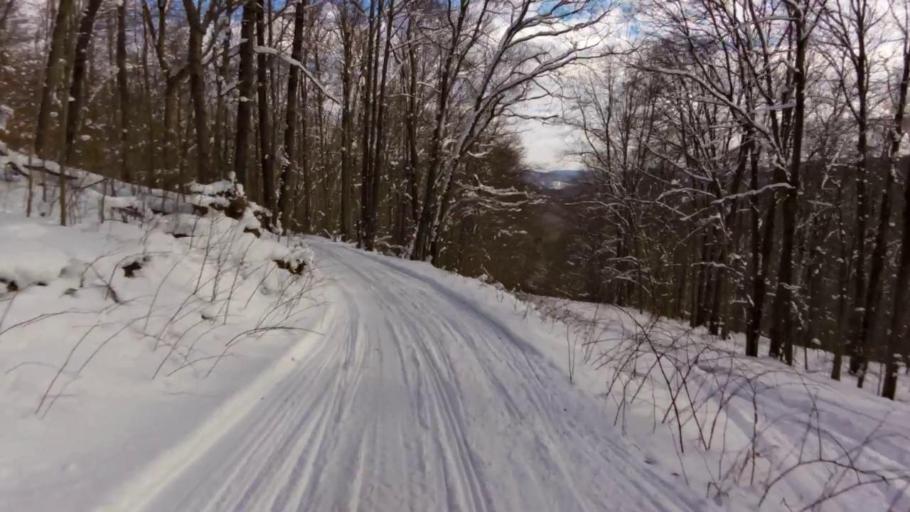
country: US
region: New York
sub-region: Cattaraugus County
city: Salamanca
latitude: 42.0609
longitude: -78.6975
